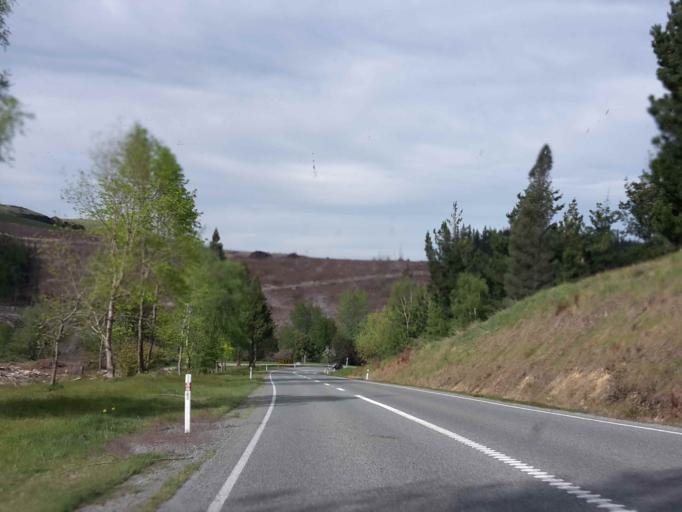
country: NZ
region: Canterbury
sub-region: Timaru District
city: Pleasant Point
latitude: -44.1243
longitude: 171.0792
